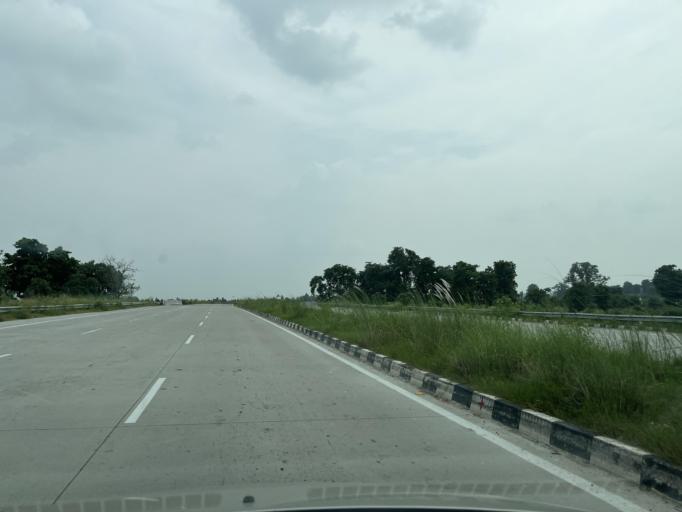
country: IN
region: Uttarakhand
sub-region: Udham Singh Nagar
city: Kashipur
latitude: 29.1905
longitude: 78.9387
